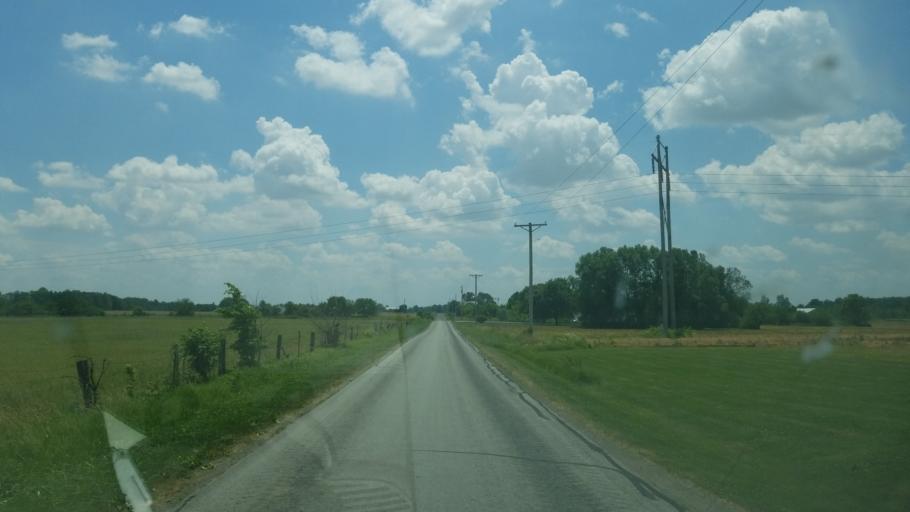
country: US
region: Ohio
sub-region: Hardin County
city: Kenton
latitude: 40.6168
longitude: -83.5593
